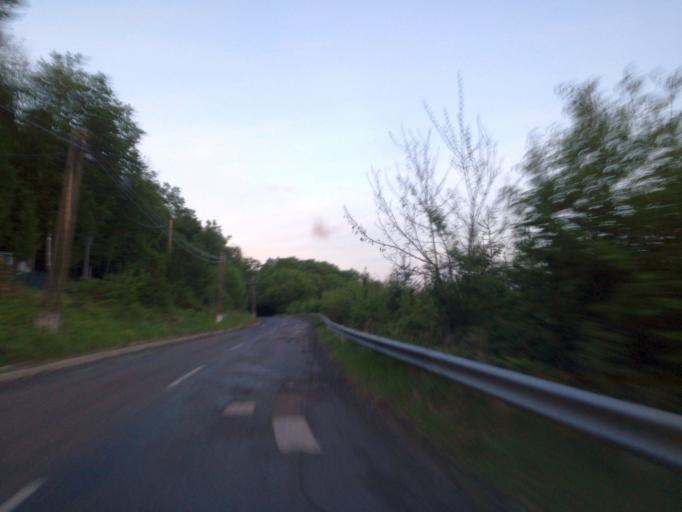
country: HU
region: Nograd
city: Batonyterenye
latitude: 47.8950
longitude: 19.8640
